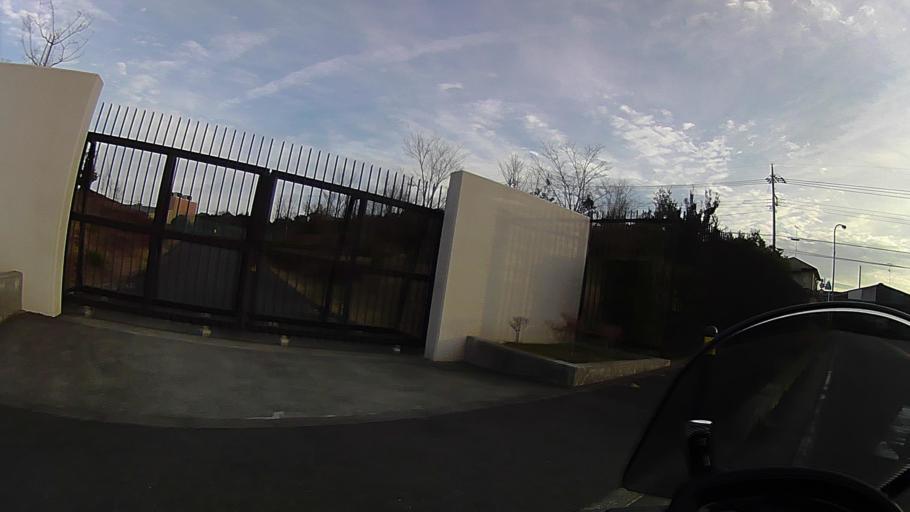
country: JP
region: Kanagawa
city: Atsugi
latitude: 35.4185
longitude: 139.4169
